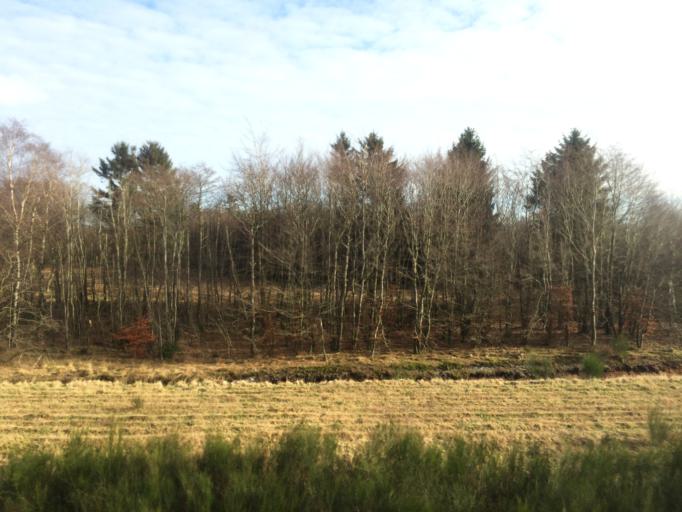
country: DK
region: South Denmark
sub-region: Vejle Kommune
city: Give
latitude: 55.8761
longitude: 9.2408
